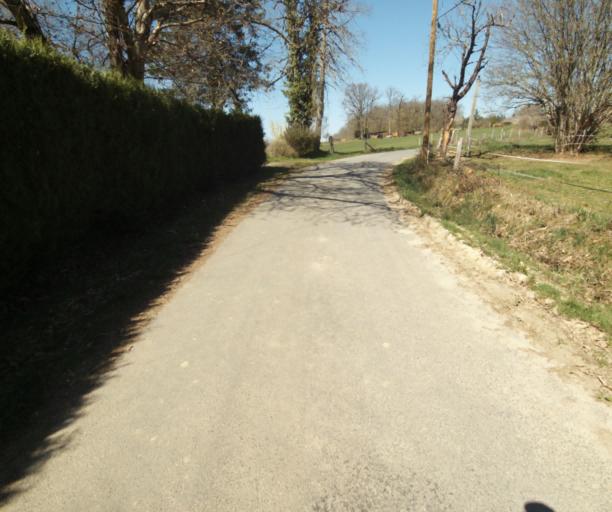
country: FR
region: Limousin
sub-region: Departement de la Correze
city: Saint-Mexant
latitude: 45.3136
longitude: 1.6572
